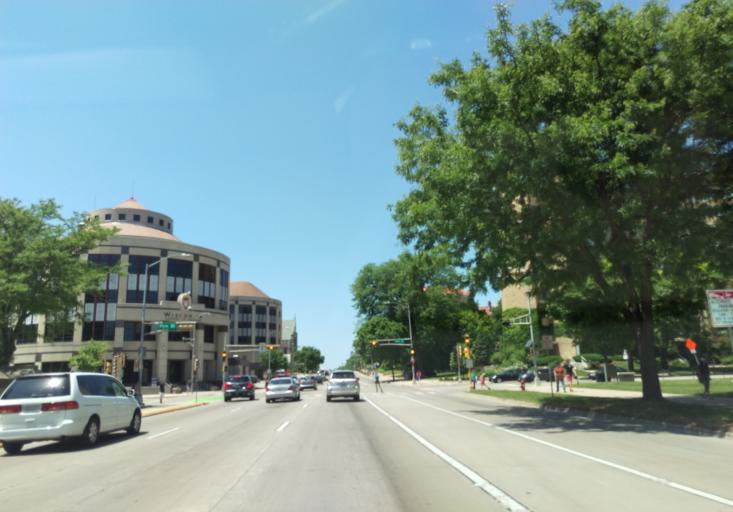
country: US
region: Wisconsin
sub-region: Dane County
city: Madison
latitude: 43.0733
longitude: -89.3999
